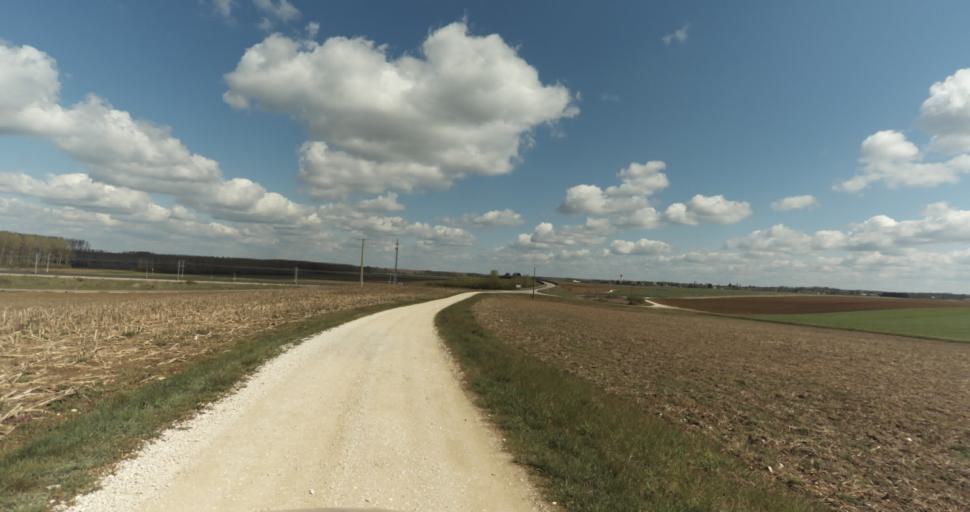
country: FR
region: Bourgogne
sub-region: Departement de la Cote-d'Or
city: Auxonne
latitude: 47.2211
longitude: 5.4231
